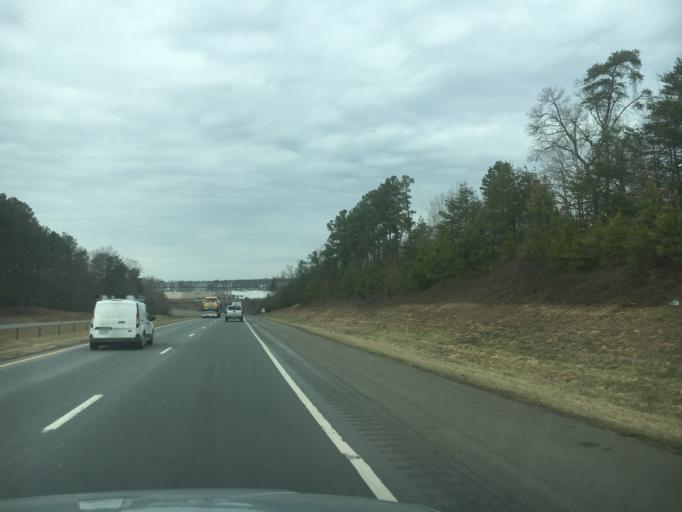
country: US
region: North Carolina
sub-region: Catawba County
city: Maiden
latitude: 35.5332
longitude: -81.2252
